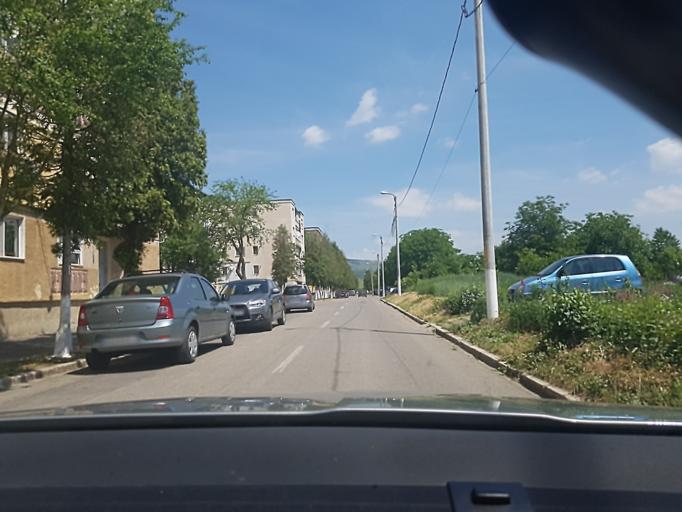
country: RO
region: Hunedoara
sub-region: Comuna Calan
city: Calan
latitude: 45.7290
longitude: 23.0290
